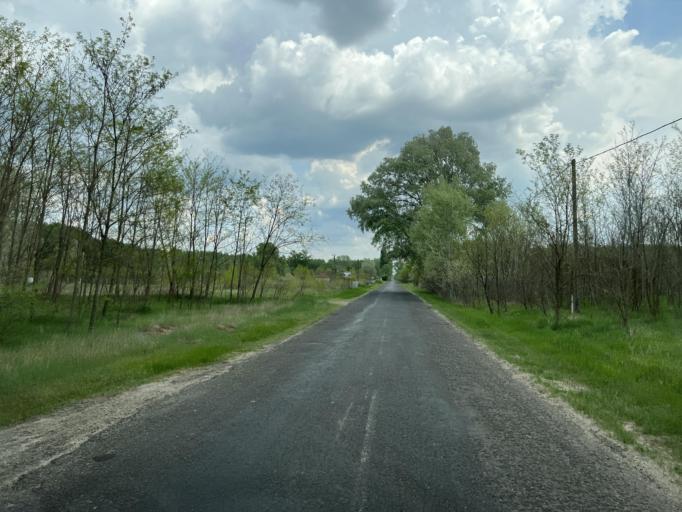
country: HU
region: Pest
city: Csemo
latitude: 47.0966
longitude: 19.7473
